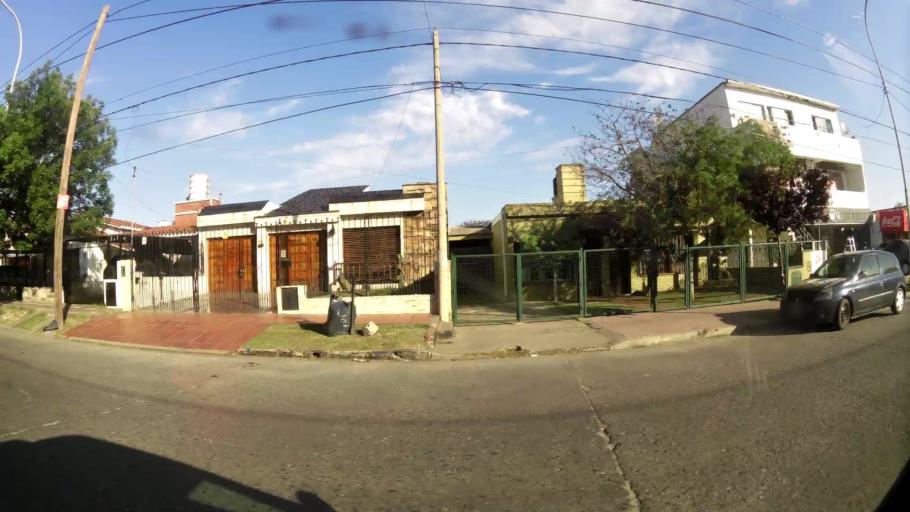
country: AR
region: Cordoba
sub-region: Departamento de Capital
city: Cordoba
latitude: -31.3847
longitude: -64.2251
